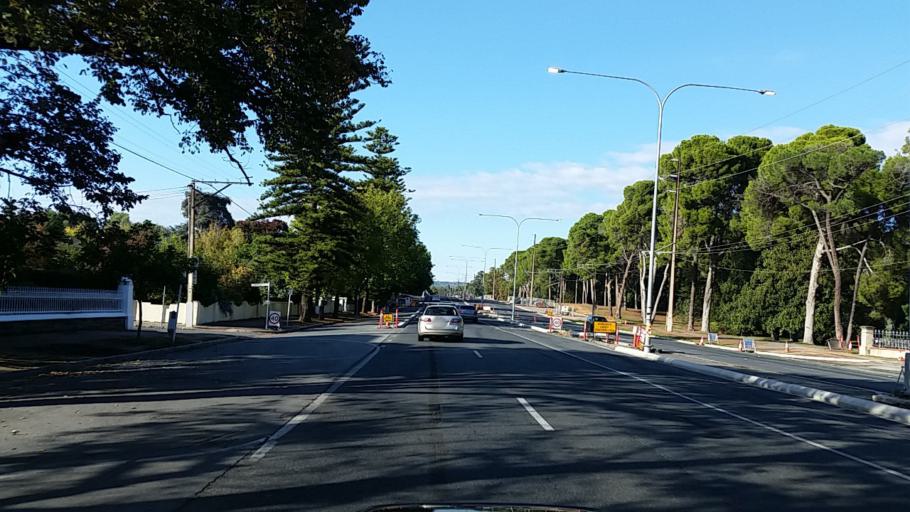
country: AU
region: South Australia
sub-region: Adelaide
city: North Adelaide
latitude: -34.9116
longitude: 138.6133
